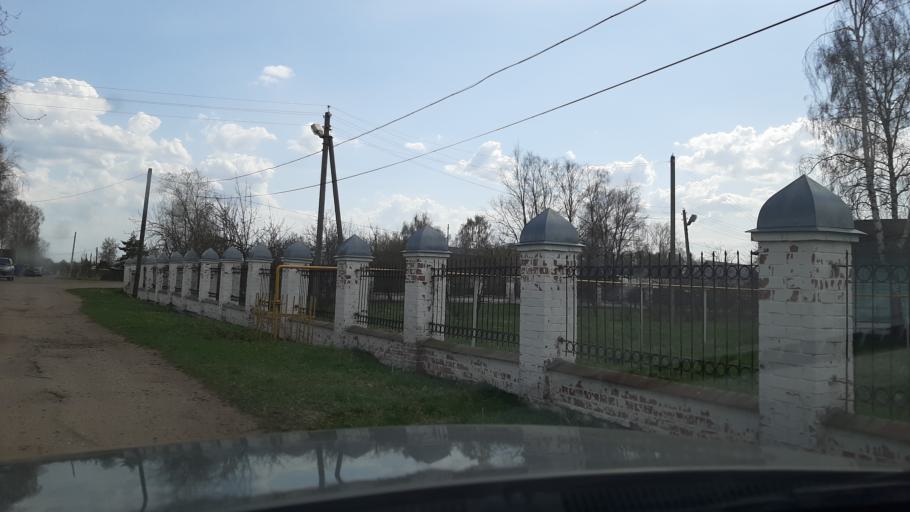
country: RU
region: Ivanovo
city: Privolzhsk
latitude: 57.3329
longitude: 41.2337
